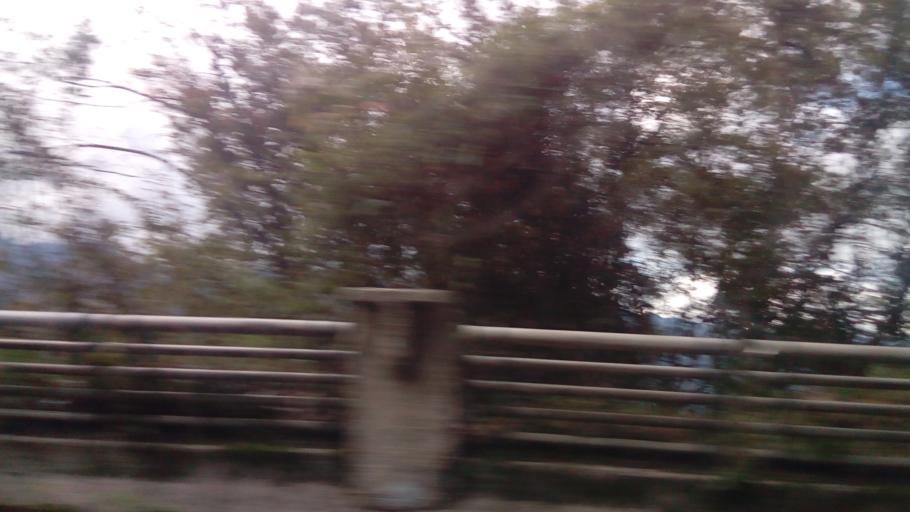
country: TW
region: Taiwan
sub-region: Nantou
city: Puli
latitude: 24.2547
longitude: 121.2488
